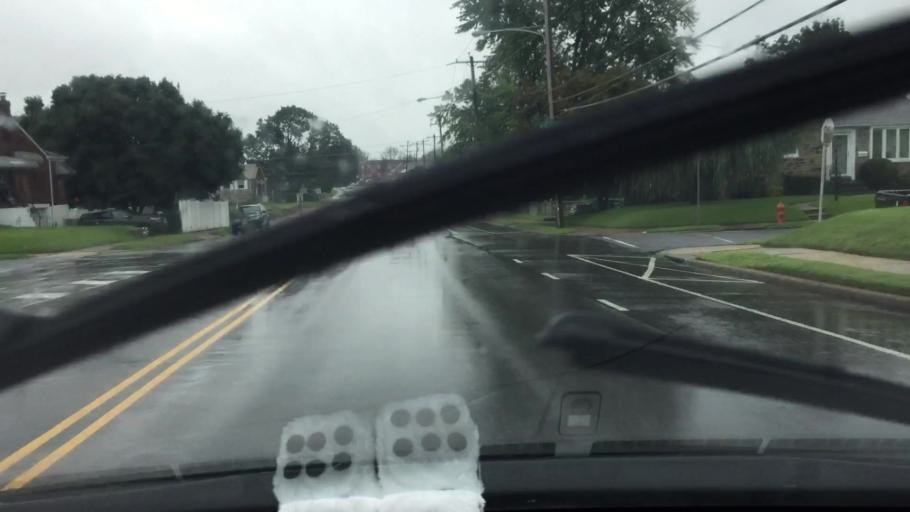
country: US
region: New Jersey
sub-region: Burlington County
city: Palmyra
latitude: 40.0514
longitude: -75.0464
